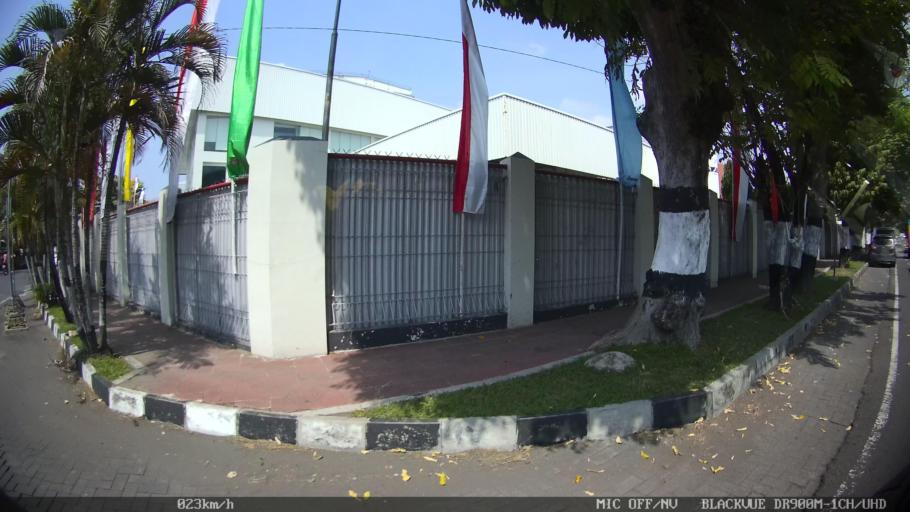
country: ID
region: Daerah Istimewa Yogyakarta
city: Yogyakarta
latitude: -7.8005
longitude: 110.3952
